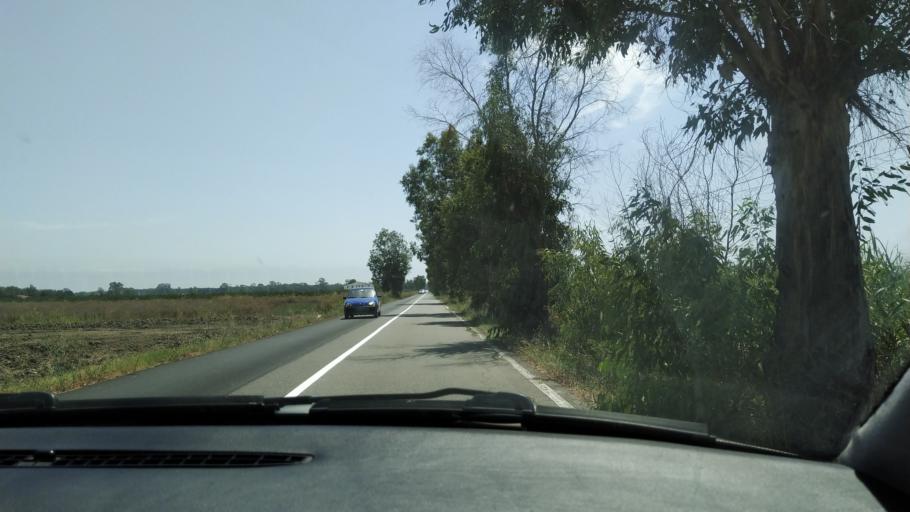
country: IT
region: Basilicate
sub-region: Provincia di Matera
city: Marconia
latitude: 40.3320
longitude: 16.7797
